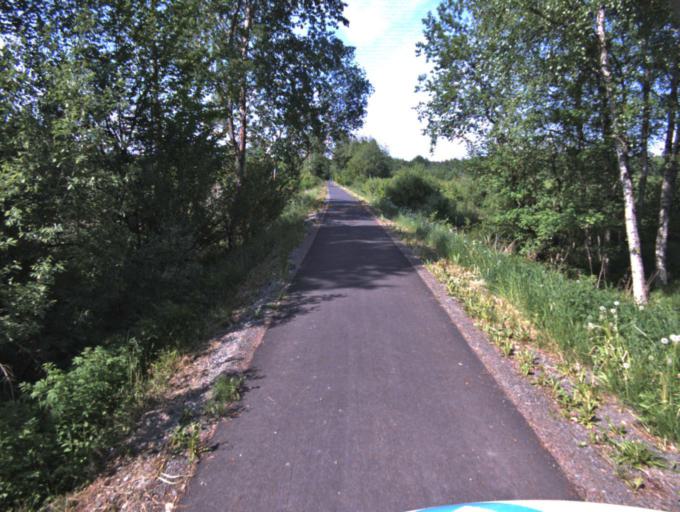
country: SE
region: Skane
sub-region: Kristianstads Kommun
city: Tollarp
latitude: 56.1935
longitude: 14.2888
